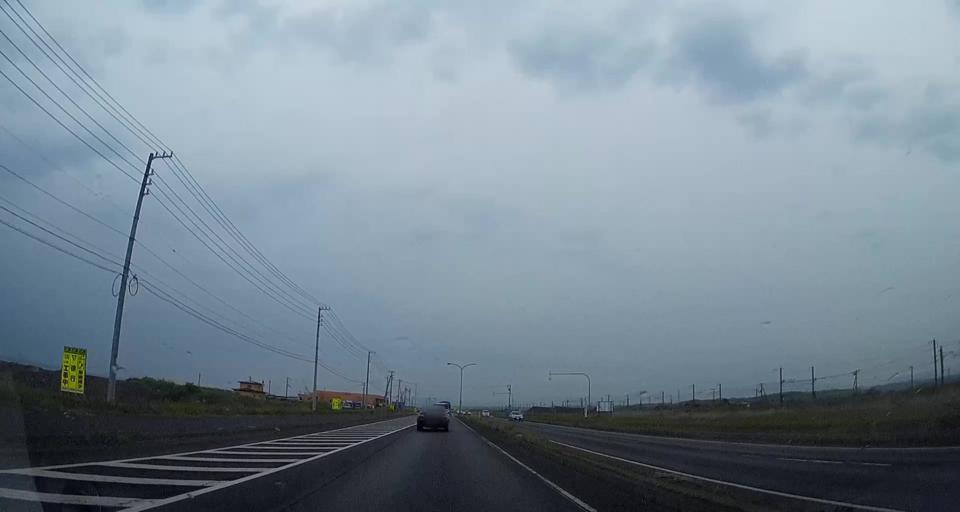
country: JP
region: Hokkaido
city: Shiraoi
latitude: 42.5904
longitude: 141.4541
